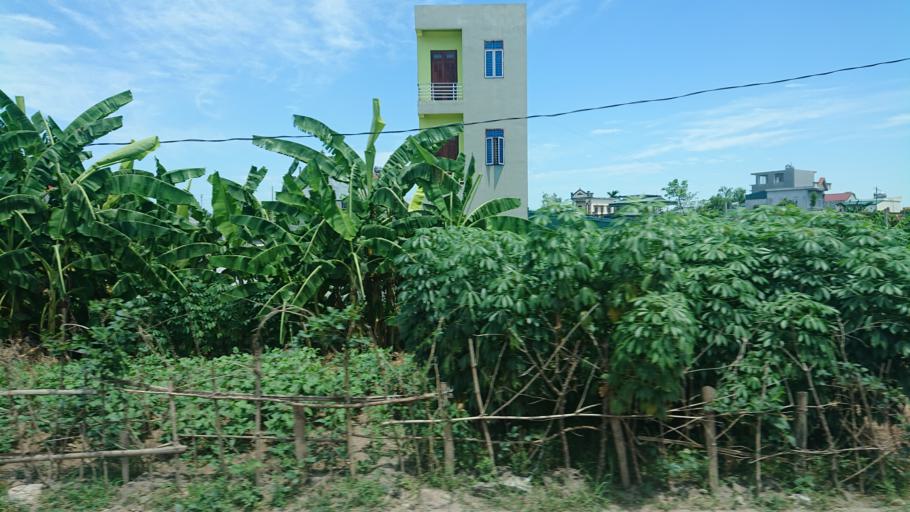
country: VN
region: Ha Nam
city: Thanh Pho Phu Ly
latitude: 20.5218
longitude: 105.9450
